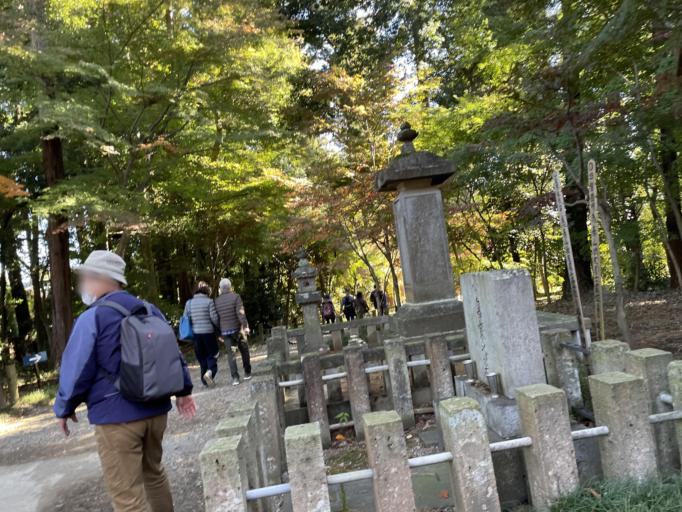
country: JP
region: Saitama
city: Asaka
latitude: 35.7897
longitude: 139.5587
